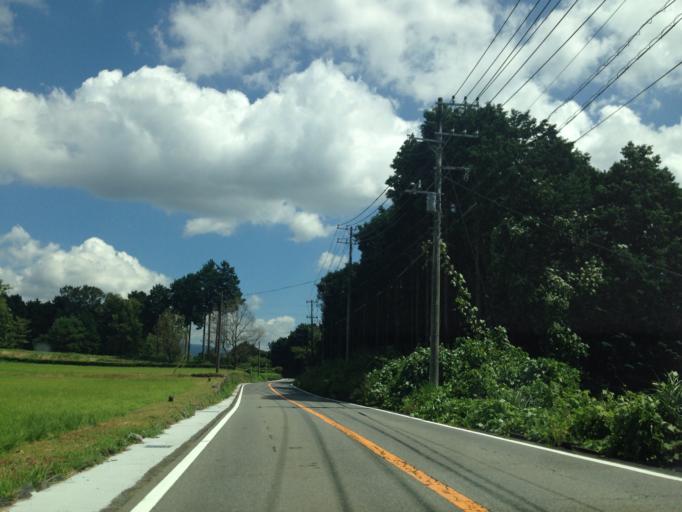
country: JP
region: Shizuoka
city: Gotemba
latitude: 35.2263
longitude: 138.8802
